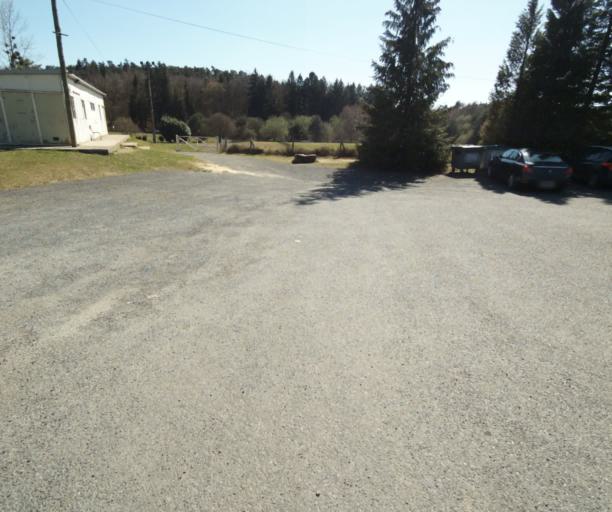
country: FR
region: Limousin
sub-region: Departement de la Correze
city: Chameyrat
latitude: 45.2682
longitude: 1.6930
